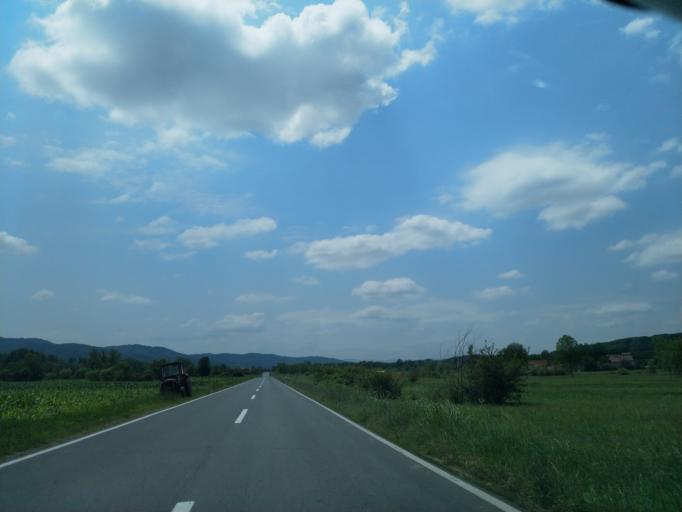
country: RS
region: Central Serbia
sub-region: Rasinski Okrug
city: Krusevac
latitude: 43.4583
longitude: 21.2439
